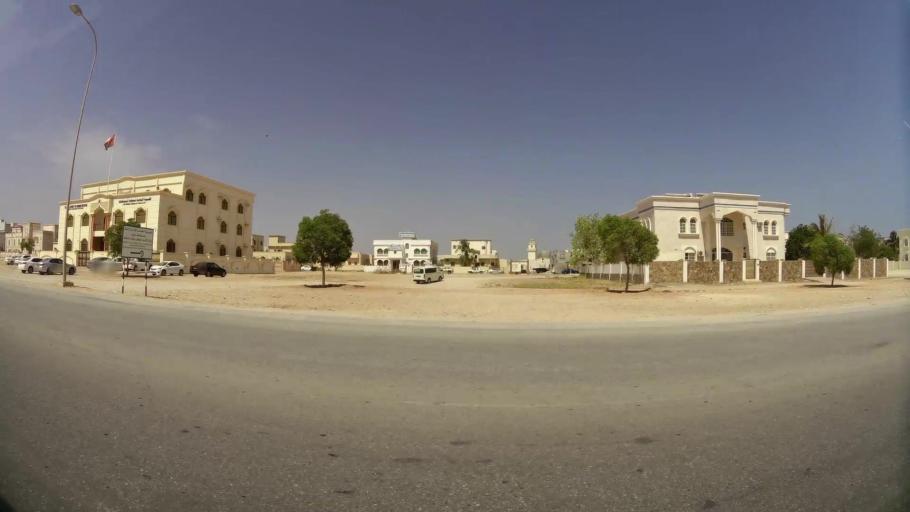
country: OM
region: Zufar
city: Salalah
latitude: 17.0483
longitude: 54.1488
